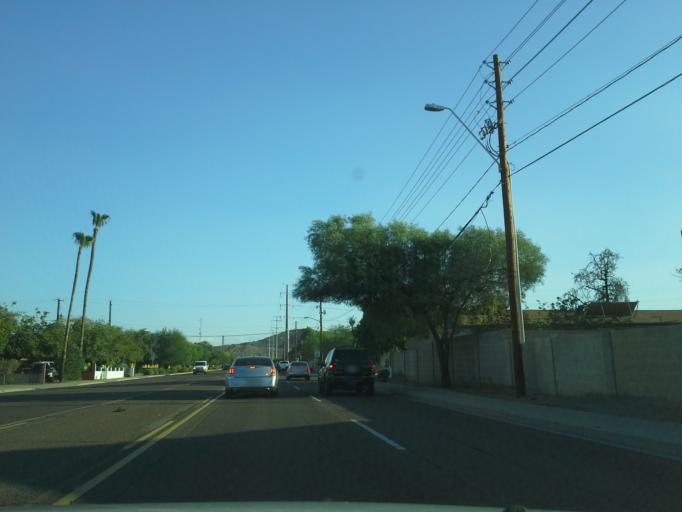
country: US
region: Arizona
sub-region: Maricopa County
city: Guadalupe
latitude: 33.3845
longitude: -111.9784
